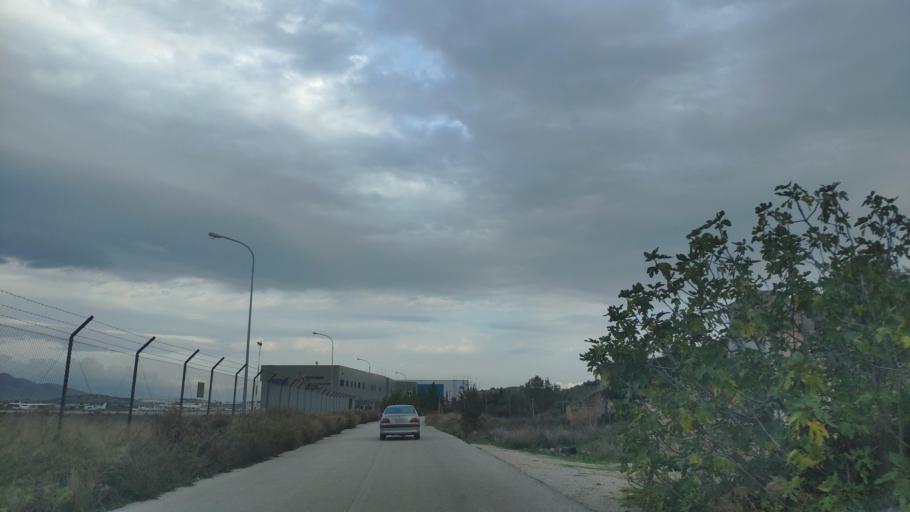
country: GR
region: Attica
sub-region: Nomarchia Dytikis Attikis
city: Megara
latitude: 37.9791
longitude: 23.3740
